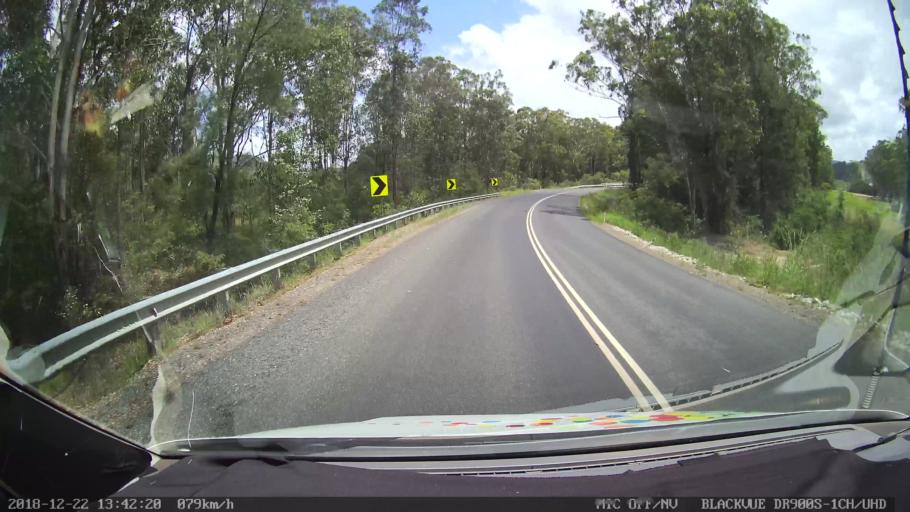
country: AU
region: New South Wales
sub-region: Clarence Valley
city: Coutts Crossing
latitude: -29.9225
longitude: 152.7544
